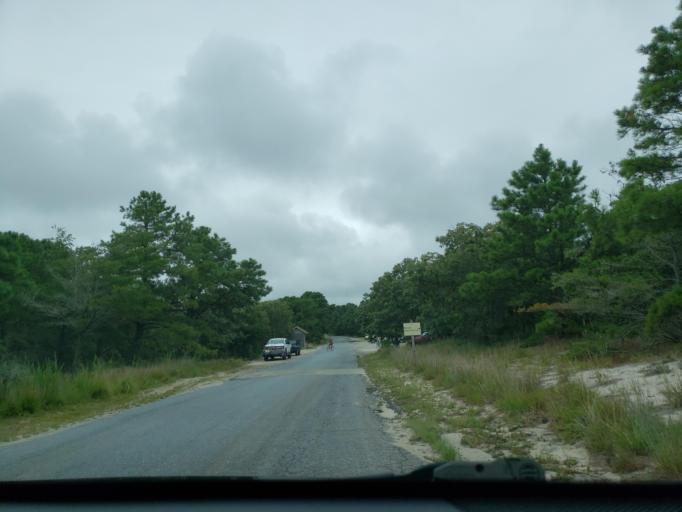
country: US
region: Delaware
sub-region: Sussex County
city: Lewes
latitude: 38.7743
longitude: -75.0877
